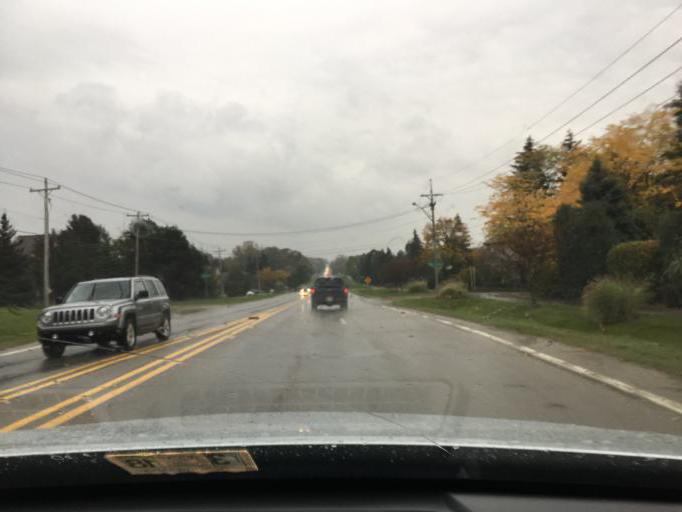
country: US
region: Michigan
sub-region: Oakland County
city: Auburn Hills
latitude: 42.7091
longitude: -83.1954
